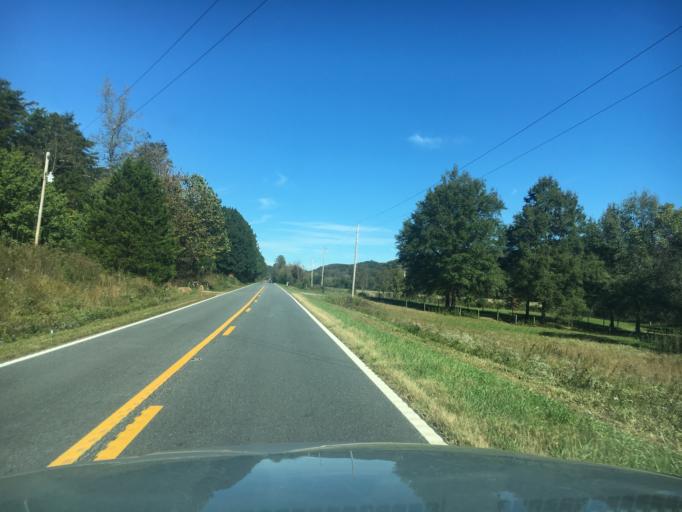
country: US
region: North Carolina
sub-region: Rutherford County
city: Spindale
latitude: 35.5173
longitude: -81.8548
